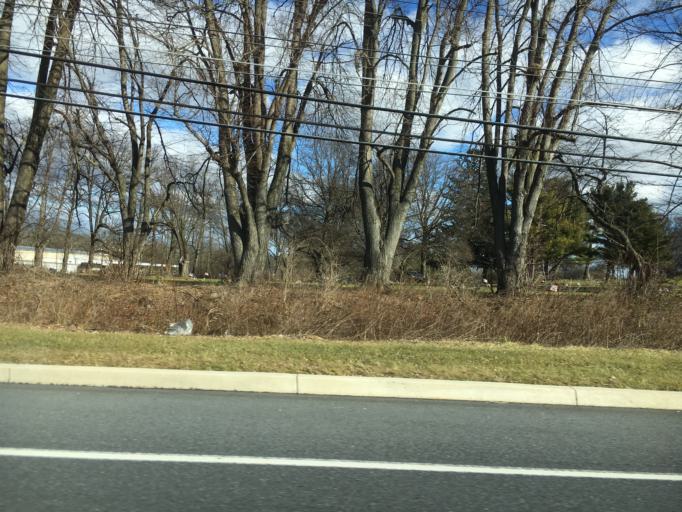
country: US
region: Pennsylvania
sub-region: Lehigh County
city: Stiles
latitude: 40.6543
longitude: -75.5056
